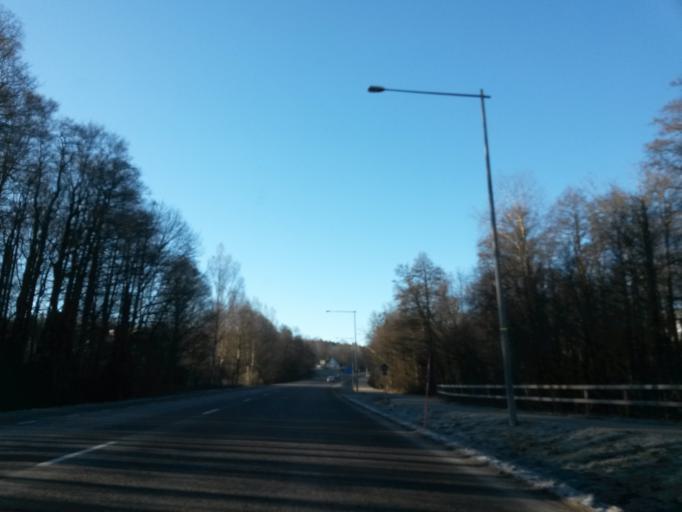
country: SE
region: Vaestra Goetaland
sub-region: Boras Kommun
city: Ganghester
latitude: 57.7967
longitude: 13.0101
